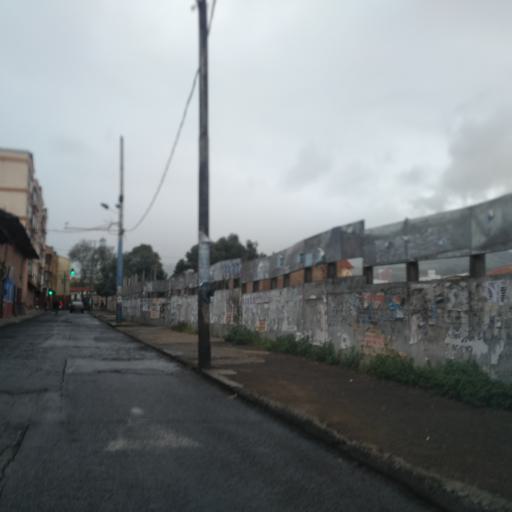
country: CO
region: Narino
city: Pasto
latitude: 1.2151
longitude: -77.2831
